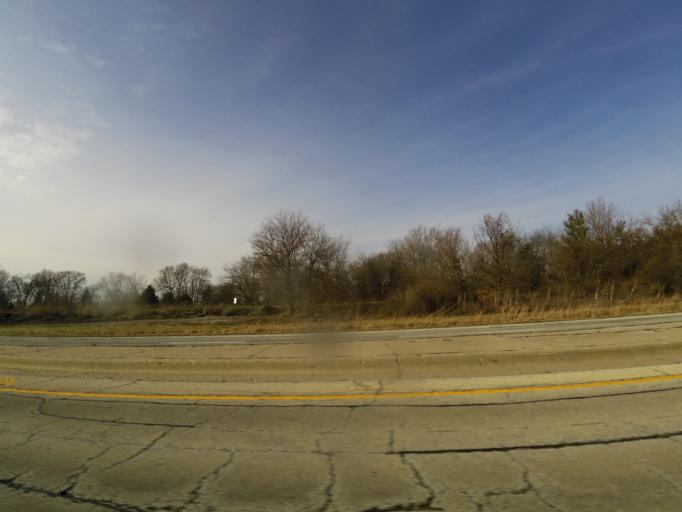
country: US
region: Illinois
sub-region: Macon County
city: Decatur
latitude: 39.7818
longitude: -88.9787
